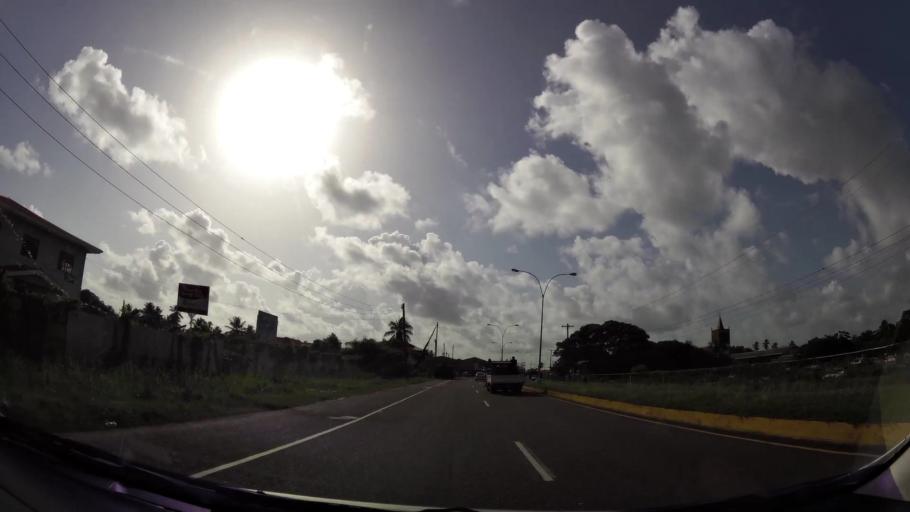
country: GY
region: Demerara-Mahaica
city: Georgetown
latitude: 6.8203
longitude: -58.0936
